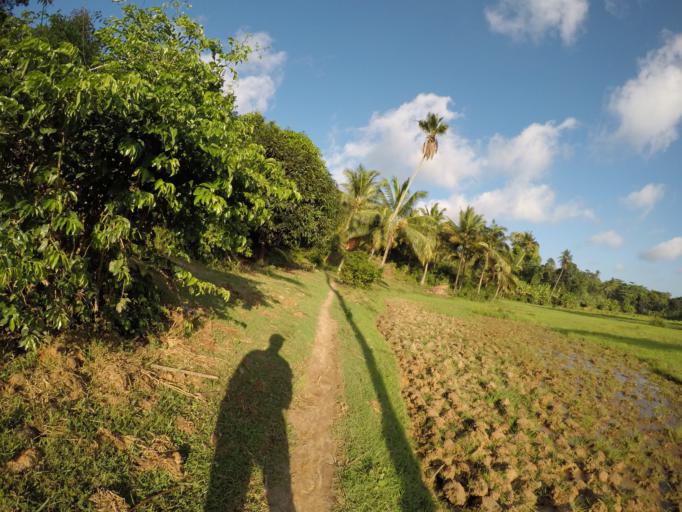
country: TZ
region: Pemba South
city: Mtambile
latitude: -5.3883
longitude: 39.7445
